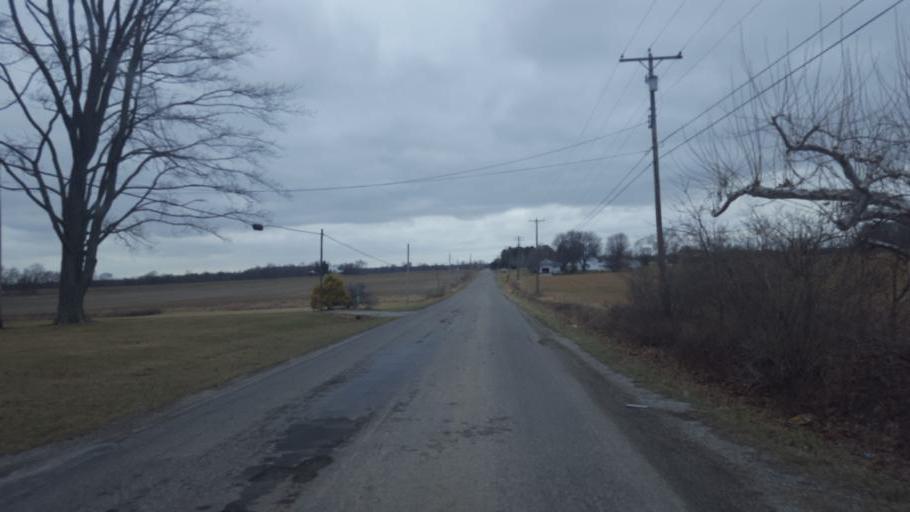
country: US
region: Ohio
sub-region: Morrow County
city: Mount Gilead
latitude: 40.5647
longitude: -82.8623
